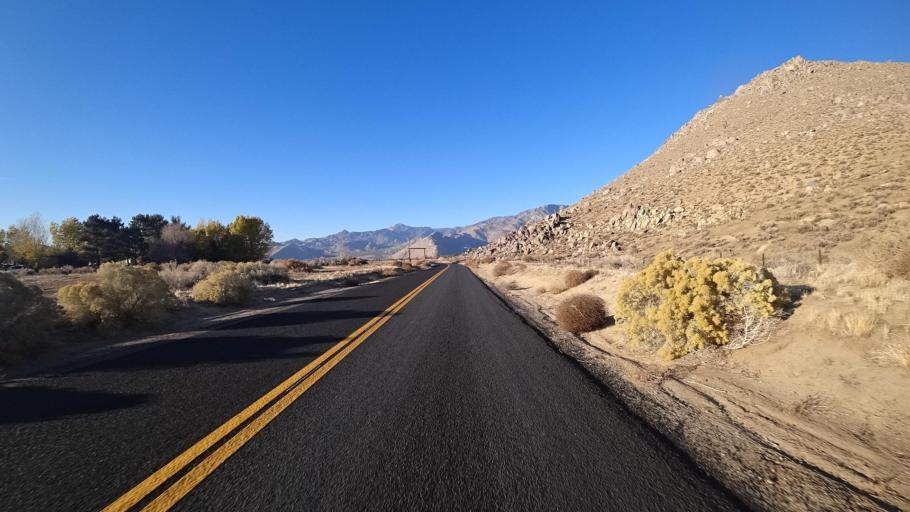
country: US
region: California
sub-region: Kern County
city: Weldon
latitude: 35.6444
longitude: -118.2499
